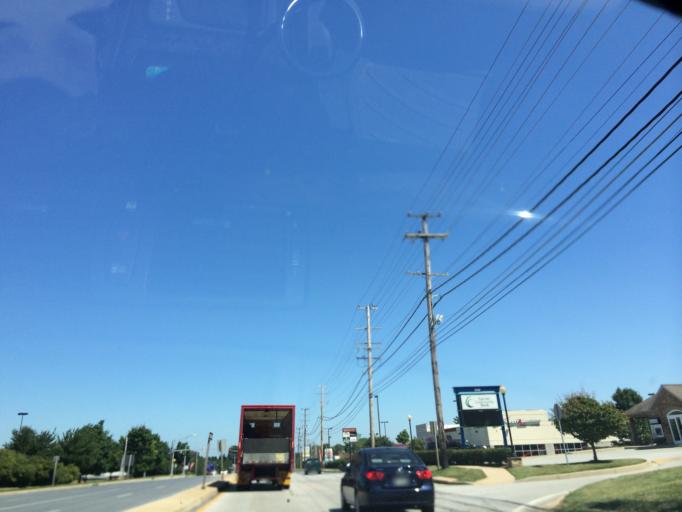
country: US
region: Maryland
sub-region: Carroll County
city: Eldersburg
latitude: 39.4037
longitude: -76.9497
